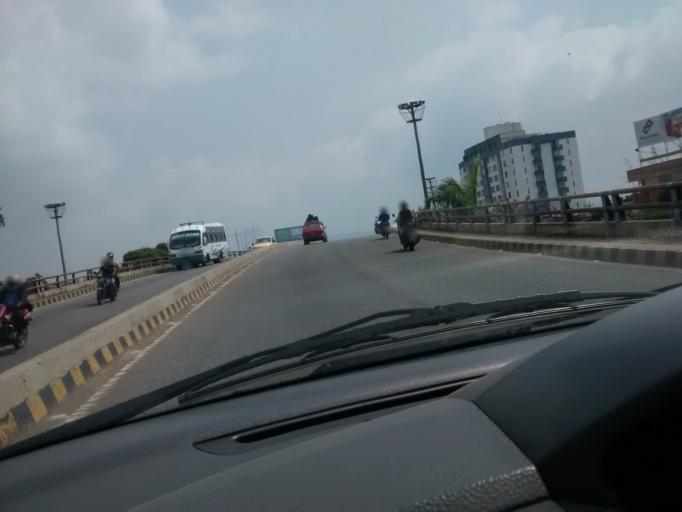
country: CO
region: Santander
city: Bucaramanga
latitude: 7.1065
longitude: -73.1138
